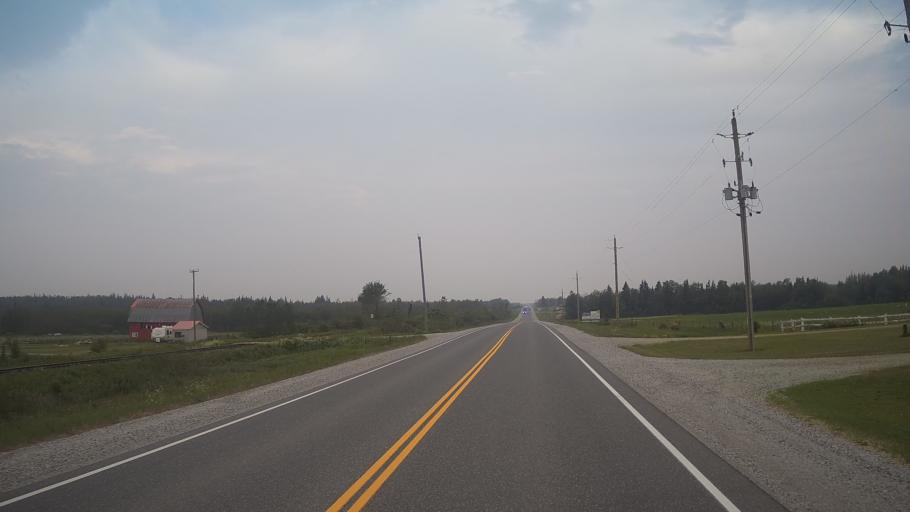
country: CA
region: Ontario
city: Hearst
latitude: 49.6719
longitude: -83.5293
